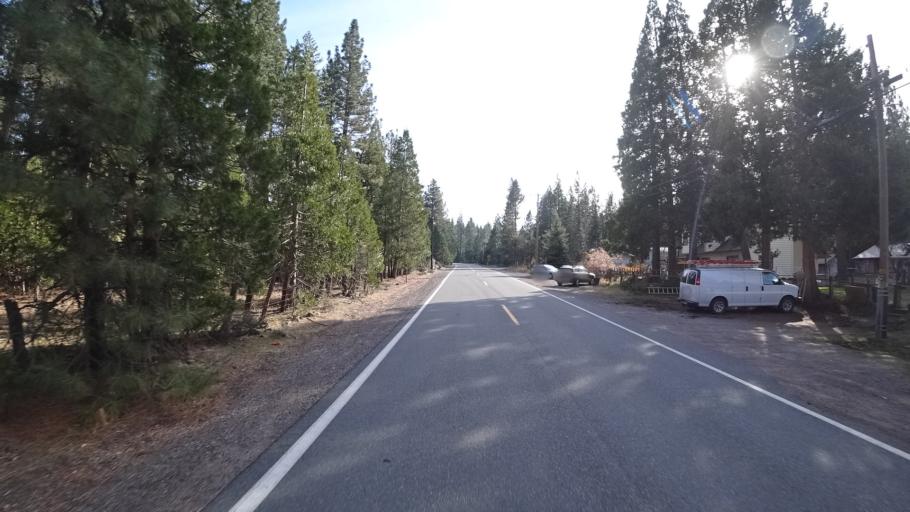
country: US
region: California
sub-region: Siskiyou County
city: Weed
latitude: 41.4095
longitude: -122.4338
